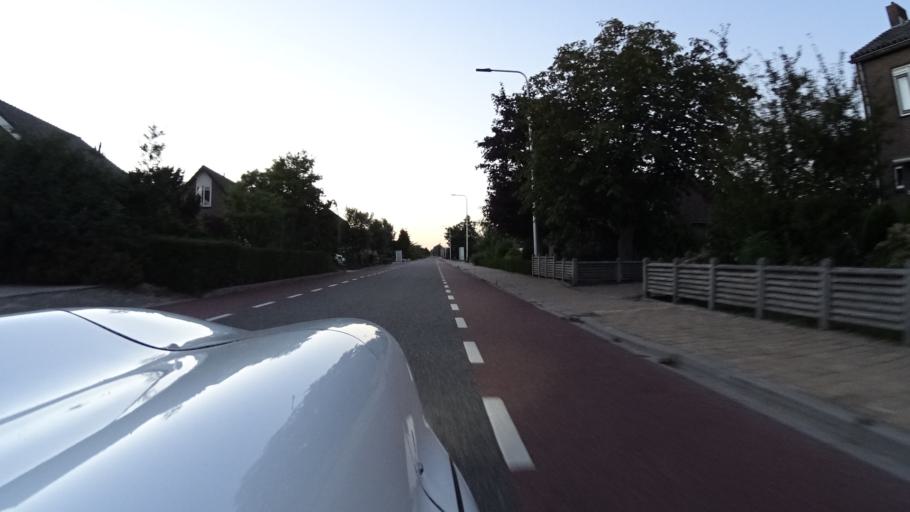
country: NL
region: South Holland
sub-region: Gemeente Kaag en Braassem
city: Oude Wetering
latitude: 52.1868
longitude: 4.6210
